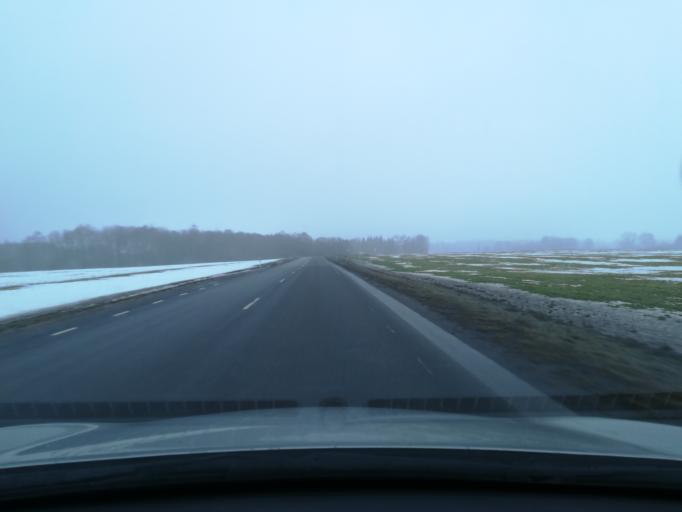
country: EE
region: Harju
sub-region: Raasiku vald
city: Arukula
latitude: 59.3658
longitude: 25.0337
